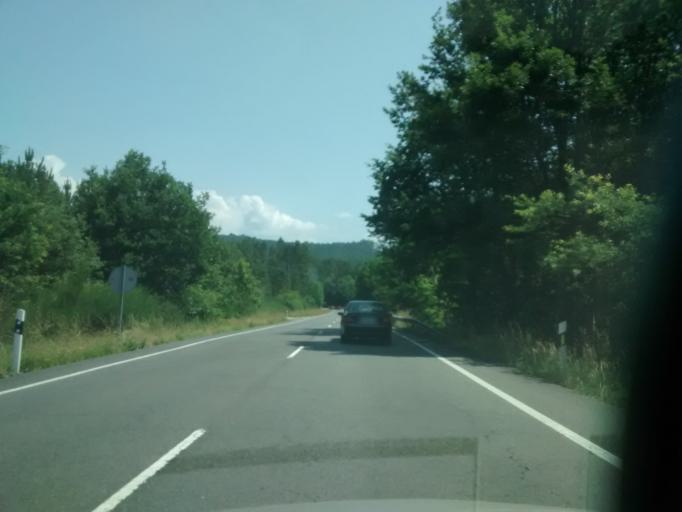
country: ES
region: Galicia
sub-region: Provincia de Ourense
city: Boboras
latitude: 42.4226
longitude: -8.1188
